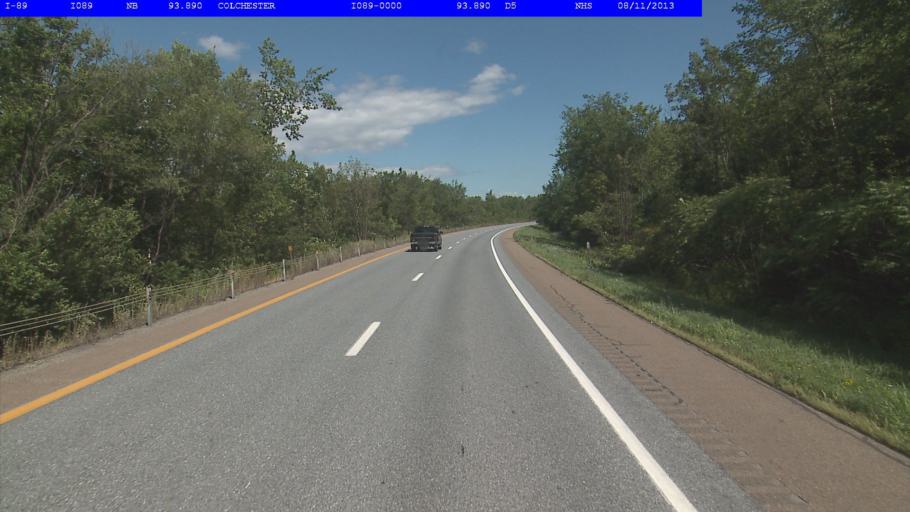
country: US
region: Vermont
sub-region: Chittenden County
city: Winooski
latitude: 44.5365
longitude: -73.1975
